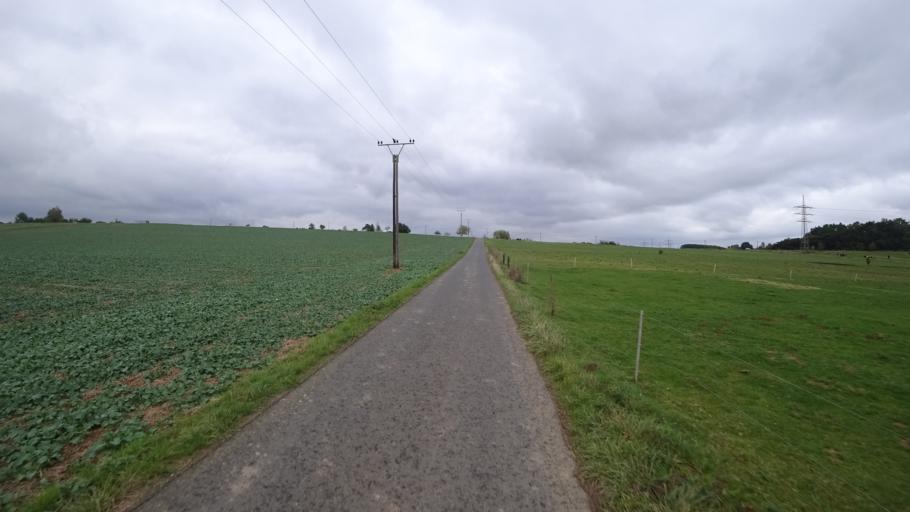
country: DE
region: Rheinland-Pfalz
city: Dierdorf
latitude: 50.5379
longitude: 7.6743
